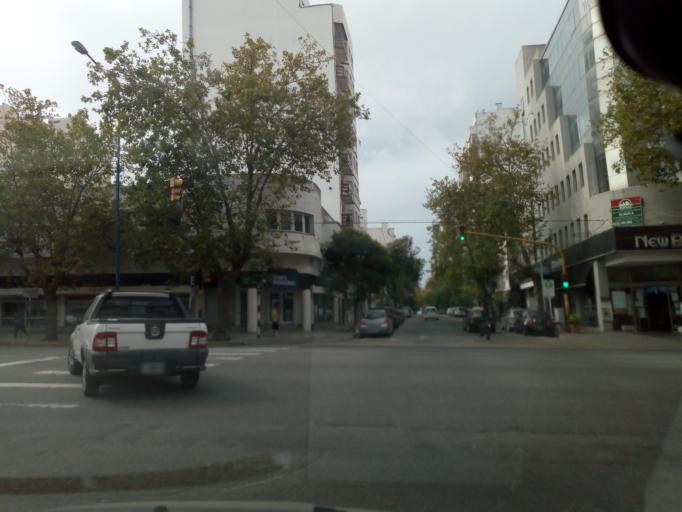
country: AR
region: Buenos Aires
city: Mar del Plata
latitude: -37.9962
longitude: -57.5513
